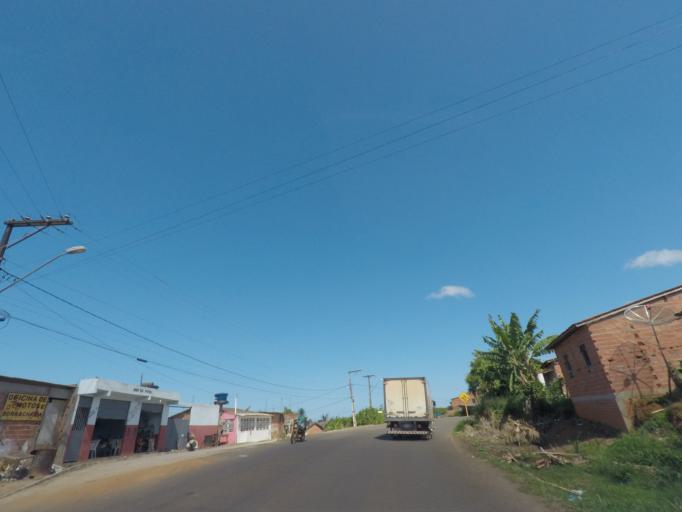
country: BR
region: Bahia
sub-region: Itubera
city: Itubera
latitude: -13.7559
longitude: -39.1524
